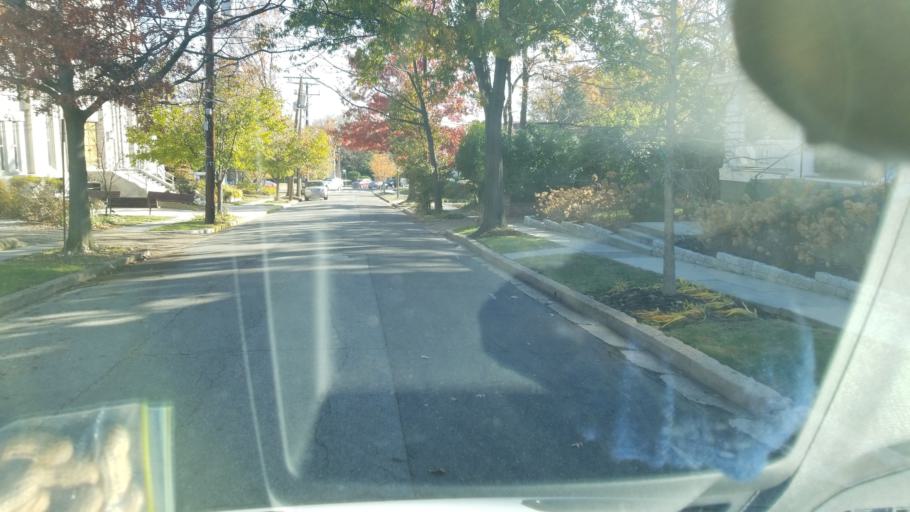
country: US
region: Maryland
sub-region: Montgomery County
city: Friendship Village
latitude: 38.9247
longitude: -77.0693
